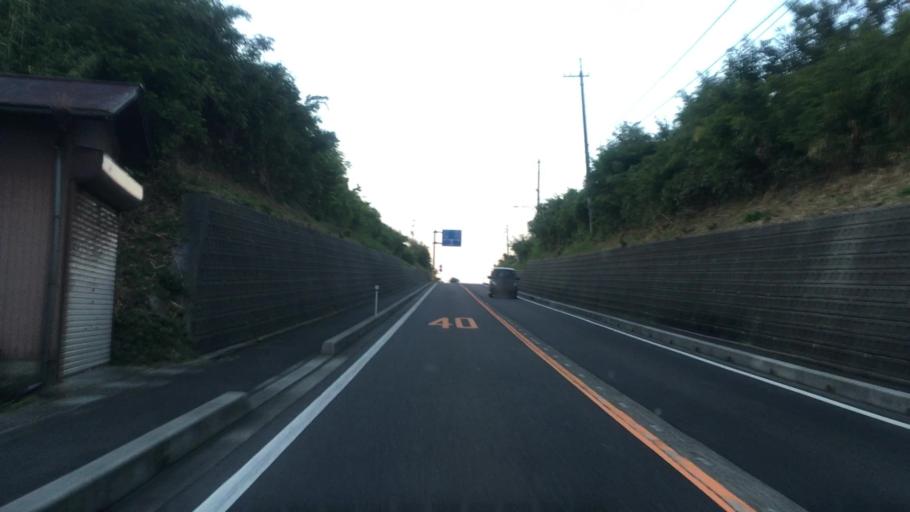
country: JP
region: Tottori
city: Tottori
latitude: 35.5870
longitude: 134.3326
